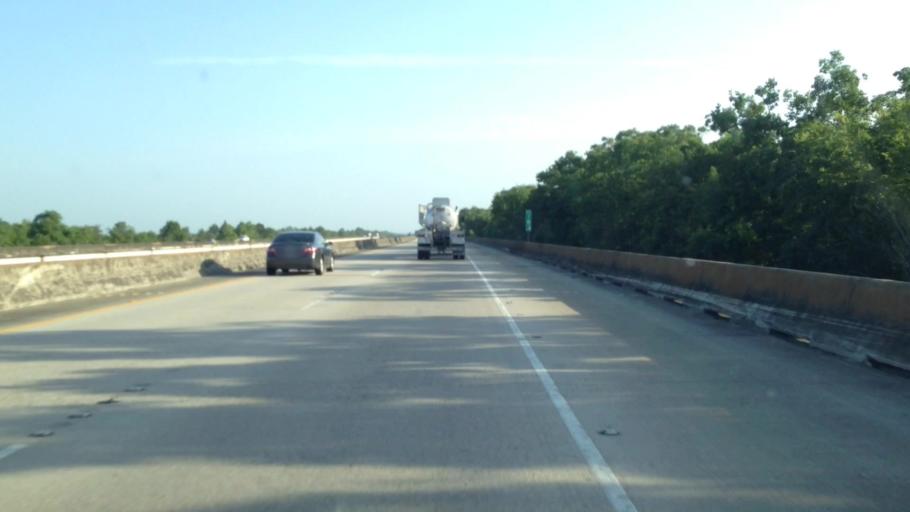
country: US
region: Louisiana
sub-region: Tangipahoa Parish
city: Ponchatoula
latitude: 30.3381
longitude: -90.4122
